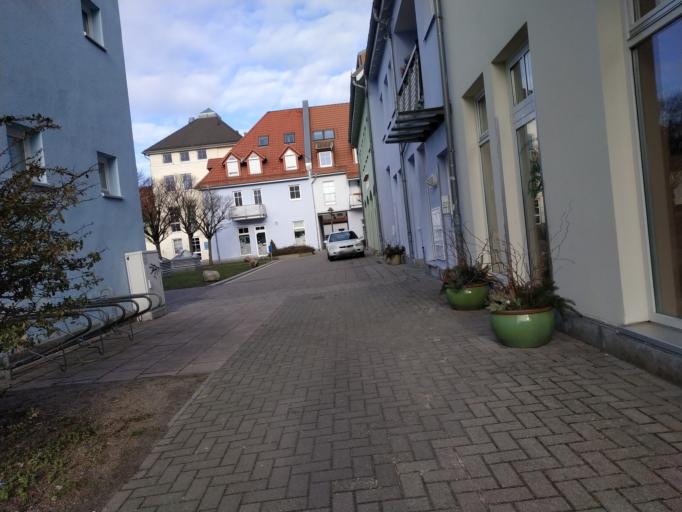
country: DE
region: Brandenburg
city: Petershagen
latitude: 52.5382
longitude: 13.8174
